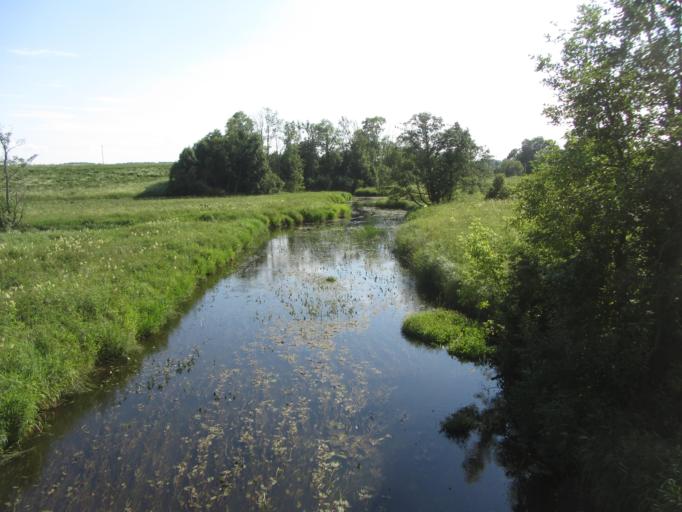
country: LT
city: Moletai
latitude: 55.3433
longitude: 25.3019
